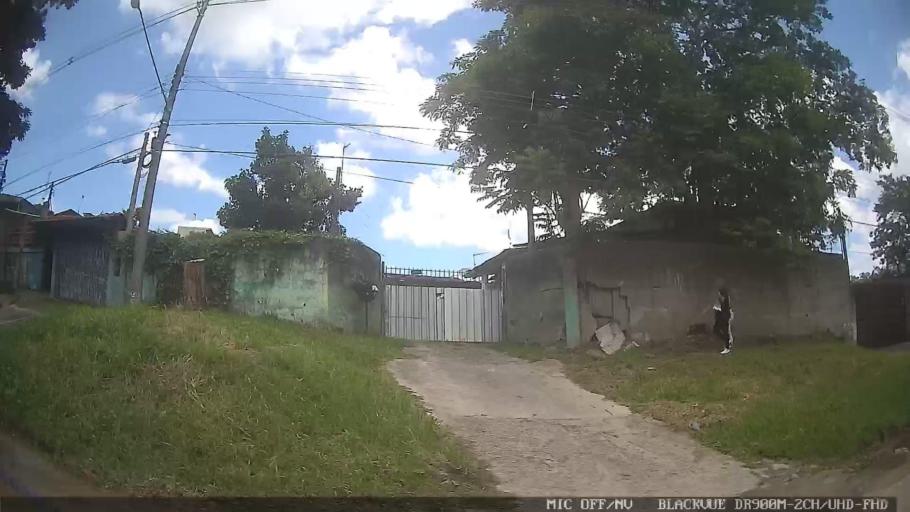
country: BR
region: Sao Paulo
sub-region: Jacarei
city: Jacarei
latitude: -23.3138
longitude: -45.9253
